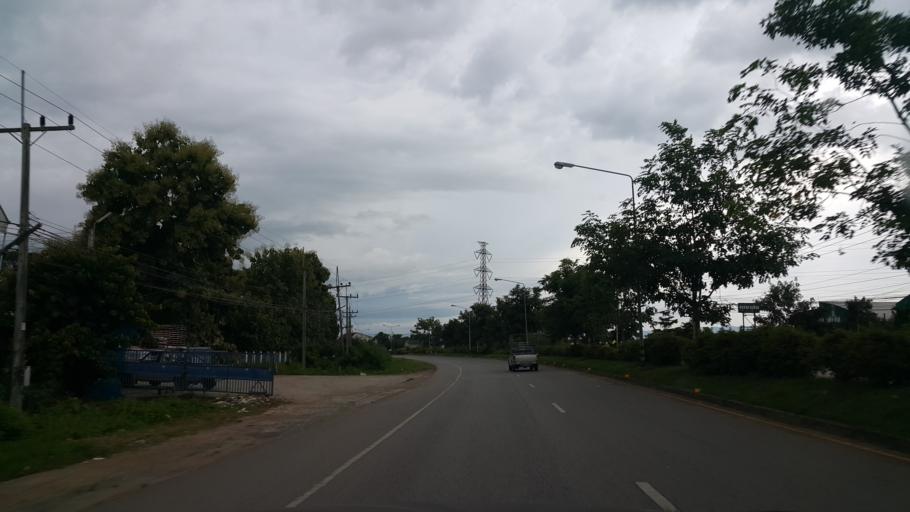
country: TH
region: Phayao
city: Phayao
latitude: 19.1444
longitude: 99.9258
